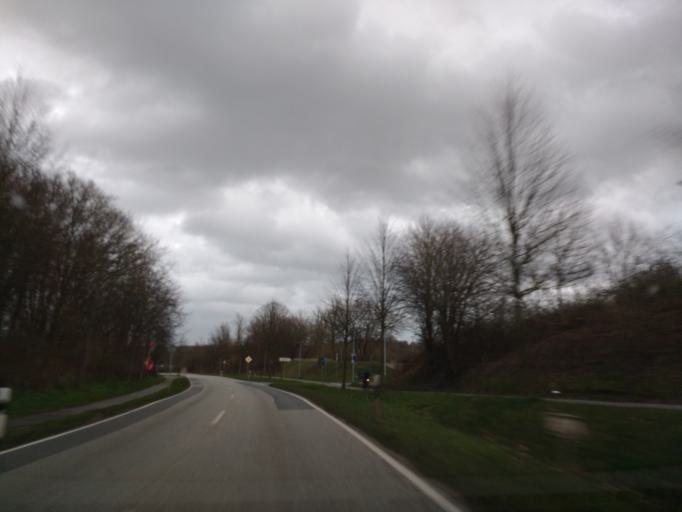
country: DE
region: Schleswig-Holstein
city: Heiligenhafen
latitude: 54.3656
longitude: 11.0006
